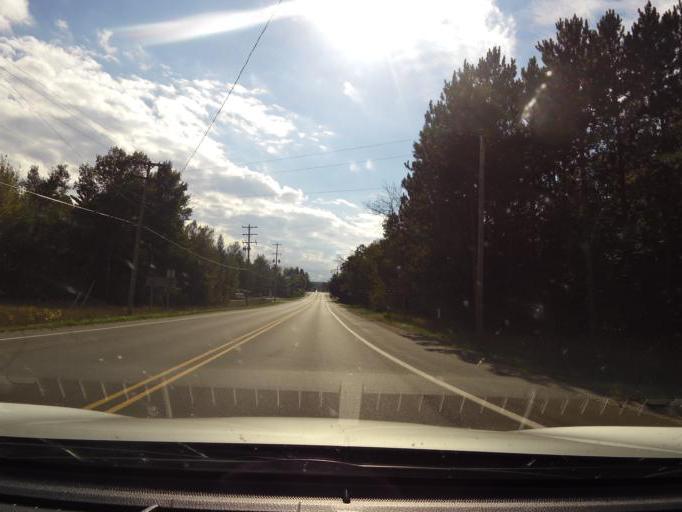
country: US
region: Michigan
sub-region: Roscommon County
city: Roscommon
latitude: 44.5027
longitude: -84.5877
